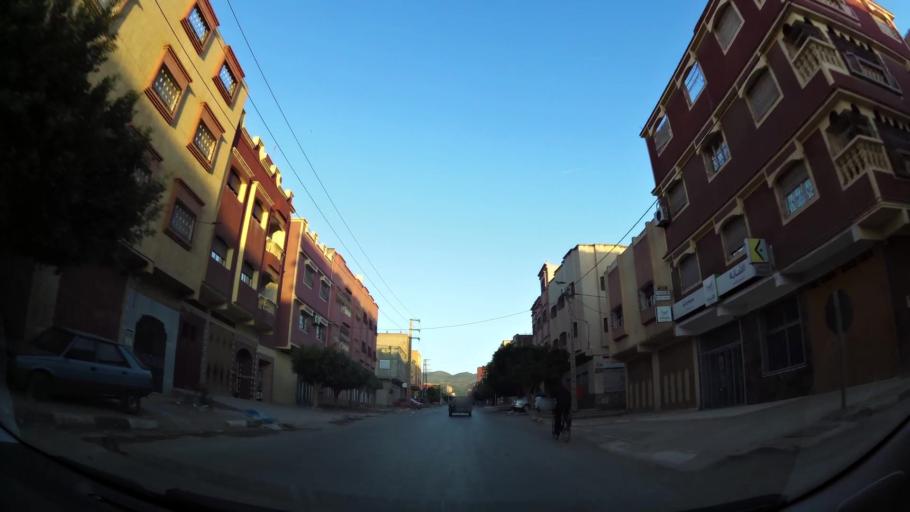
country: MA
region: Oriental
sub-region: Berkane-Taourirt
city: Berkane
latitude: 34.9122
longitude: -2.3181
